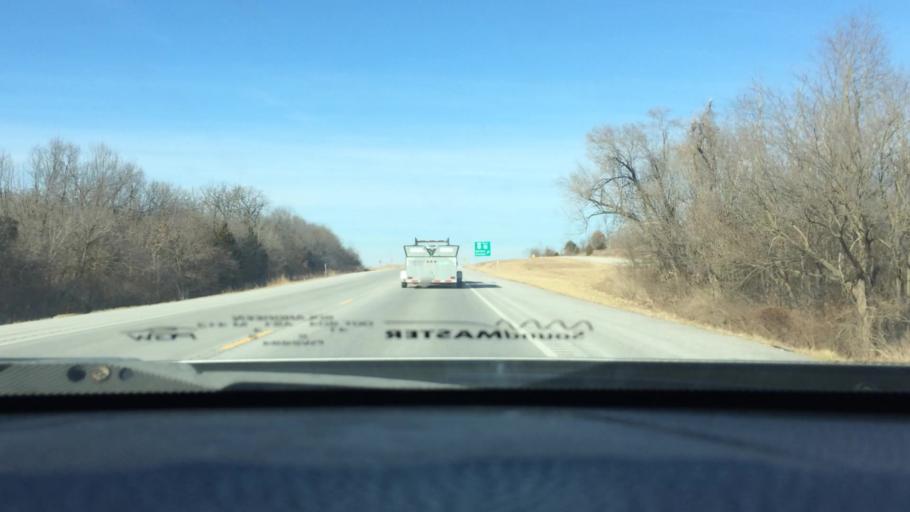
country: US
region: Missouri
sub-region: Newton County
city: Neosho
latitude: 36.8981
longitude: -94.3169
